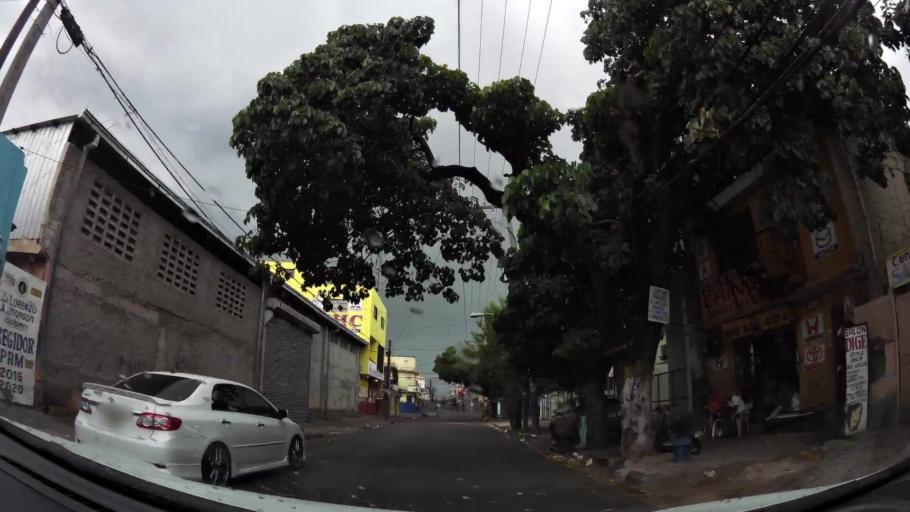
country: DO
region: Nacional
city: San Carlos
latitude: 18.4902
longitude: -69.9078
